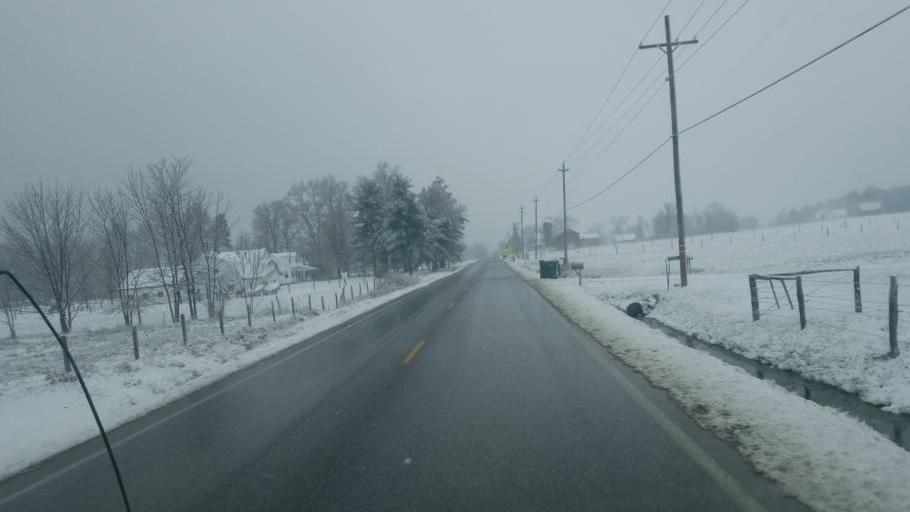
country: US
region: Ohio
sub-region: Geauga County
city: Middlefield
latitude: 41.4185
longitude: -81.1015
